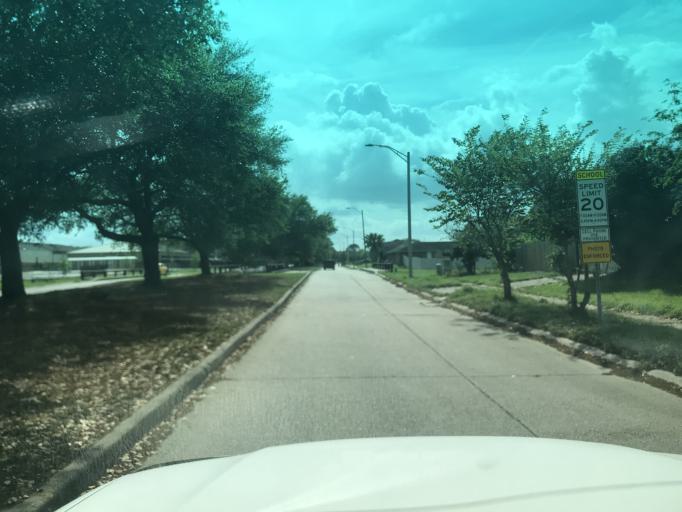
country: US
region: Louisiana
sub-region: Saint Bernard Parish
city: Chalmette
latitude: 30.0370
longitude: -89.9580
